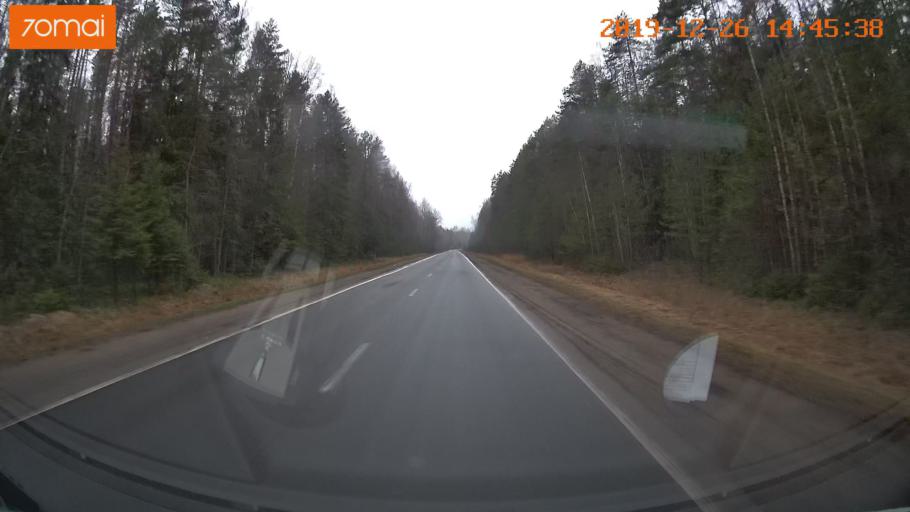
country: RU
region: Jaroslavl
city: Poshekhon'ye
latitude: 58.3370
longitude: 39.0350
